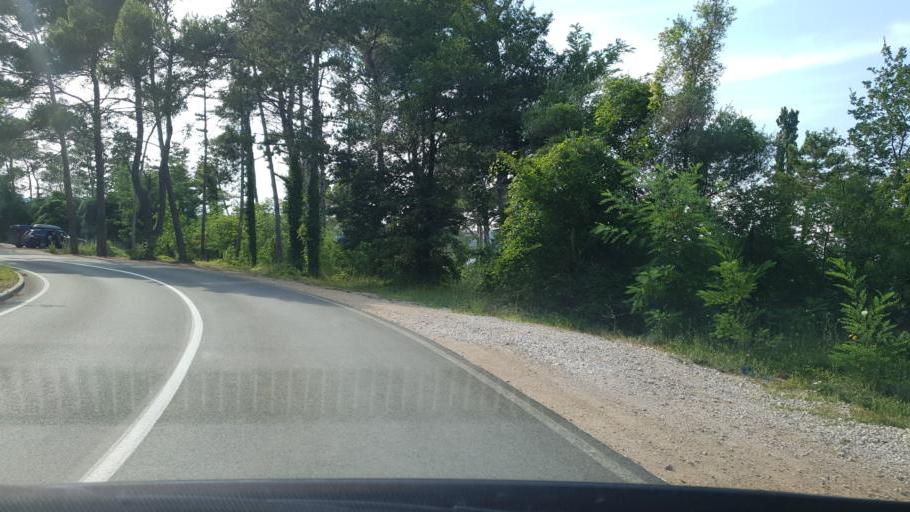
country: HR
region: Primorsko-Goranska
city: Njivice
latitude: 45.1519
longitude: 14.6148
